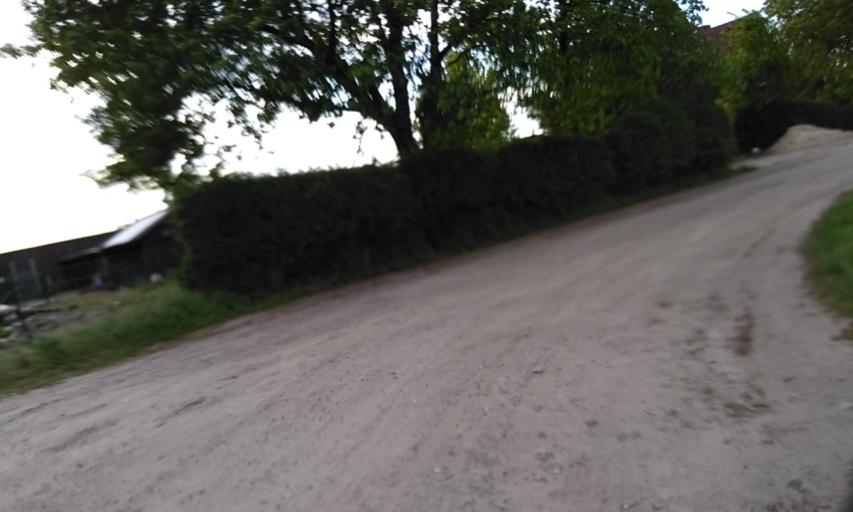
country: DE
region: Lower Saxony
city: Harsefeld
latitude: 53.4546
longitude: 9.5334
